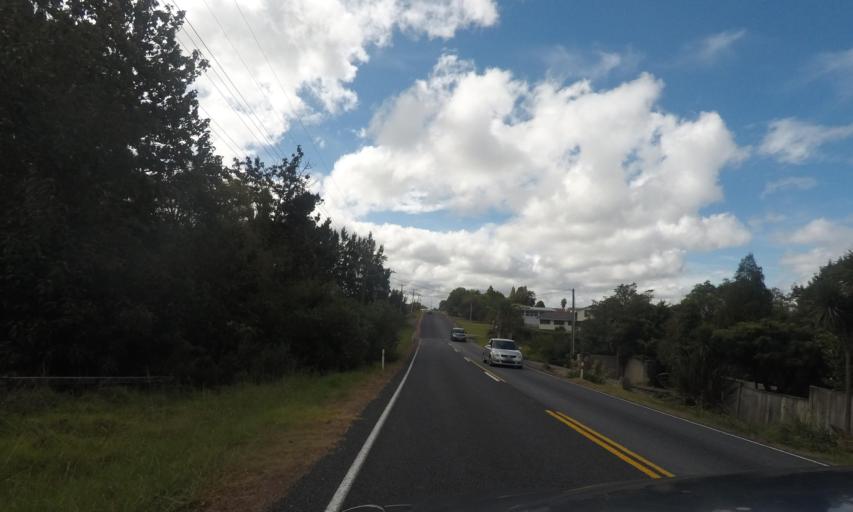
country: NZ
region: Auckland
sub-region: Auckland
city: Rosebank
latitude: -36.7951
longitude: 174.6369
